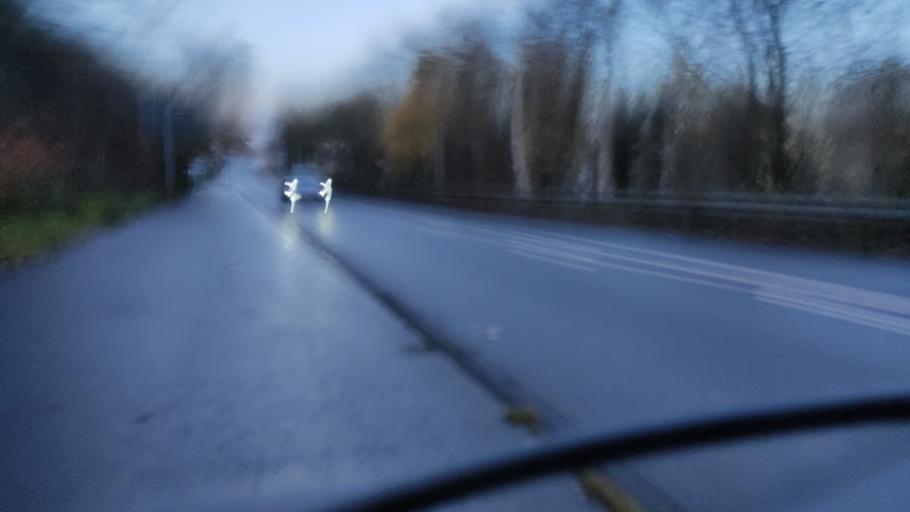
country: DE
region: North Rhine-Westphalia
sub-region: Regierungsbezirk Dusseldorf
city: Velbert
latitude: 51.3878
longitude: 7.0802
